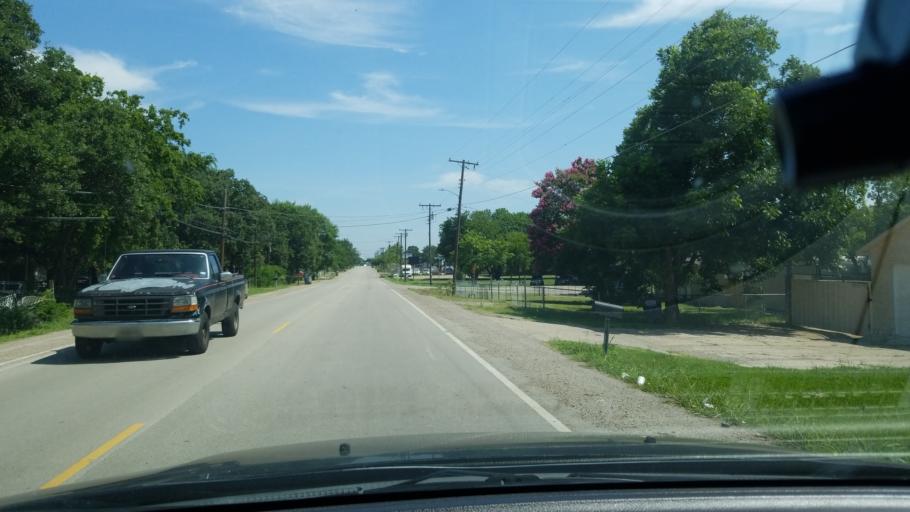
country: US
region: Texas
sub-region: Dallas County
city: Balch Springs
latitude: 32.7272
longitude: -96.6313
